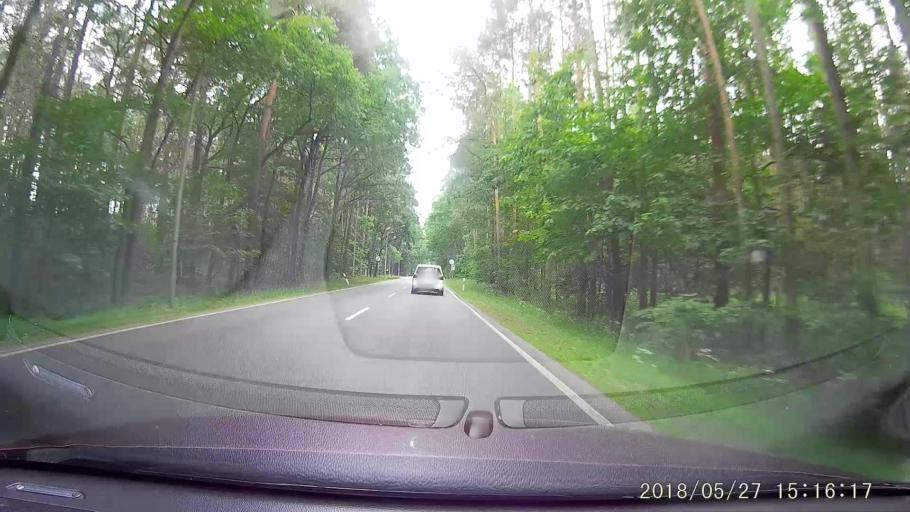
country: DE
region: Saxony
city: Niesky
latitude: 51.2781
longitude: 14.8218
